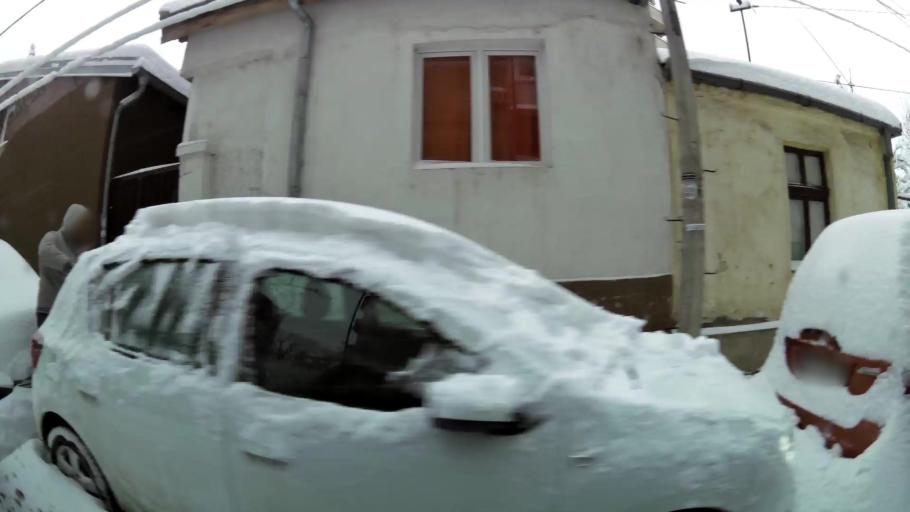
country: RS
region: Central Serbia
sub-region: Belgrade
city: Vracar
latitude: 44.7924
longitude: 20.4761
